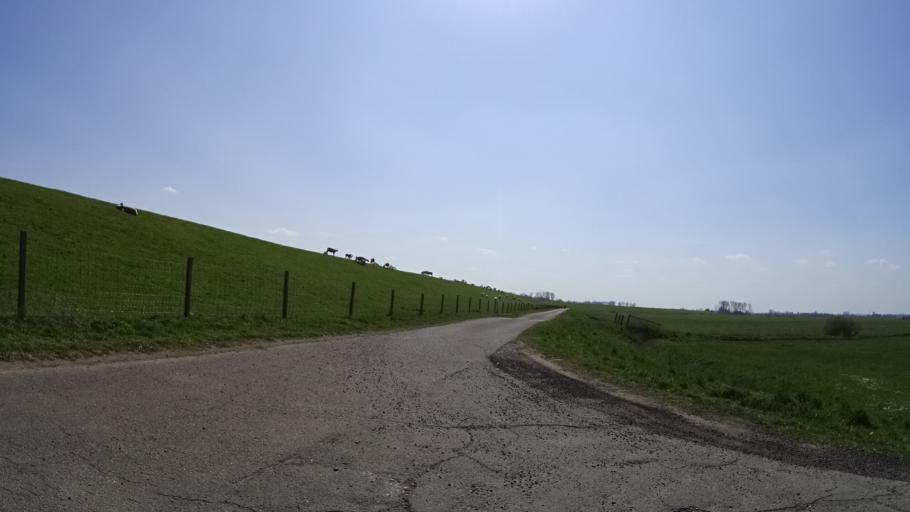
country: DE
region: Lower Saxony
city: Weener
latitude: 53.1445
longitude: 7.3696
